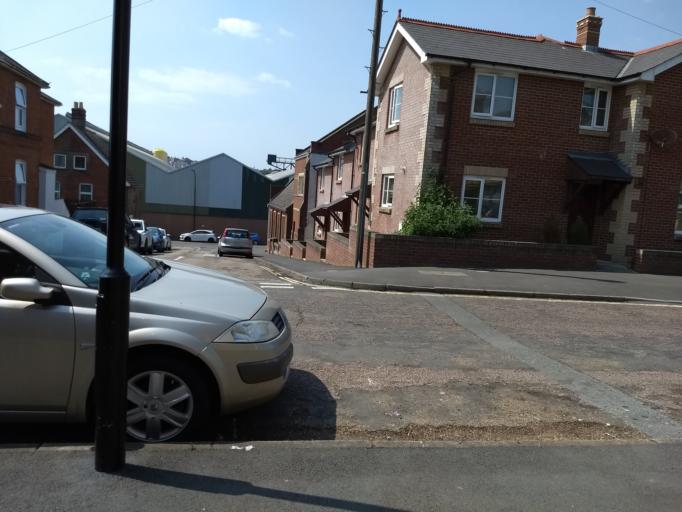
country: GB
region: England
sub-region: Isle of Wight
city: East Cowes
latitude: 50.7554
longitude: -1.2883
